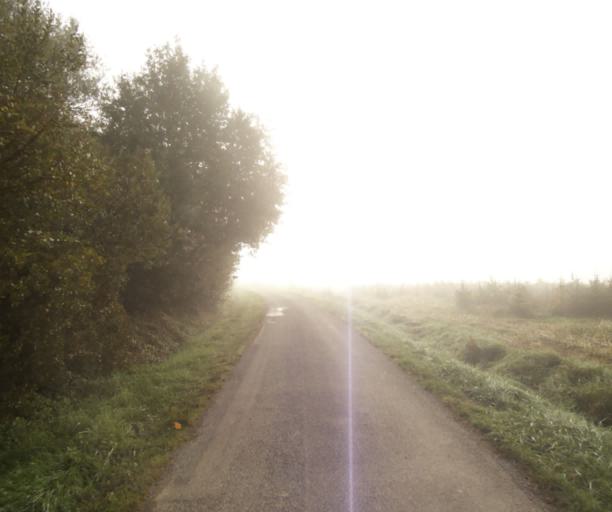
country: FR
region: Midi-Pyrenees
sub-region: Departement du Tarn-et-Garonne
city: Nohic
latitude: 43.8922
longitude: 1.4521
